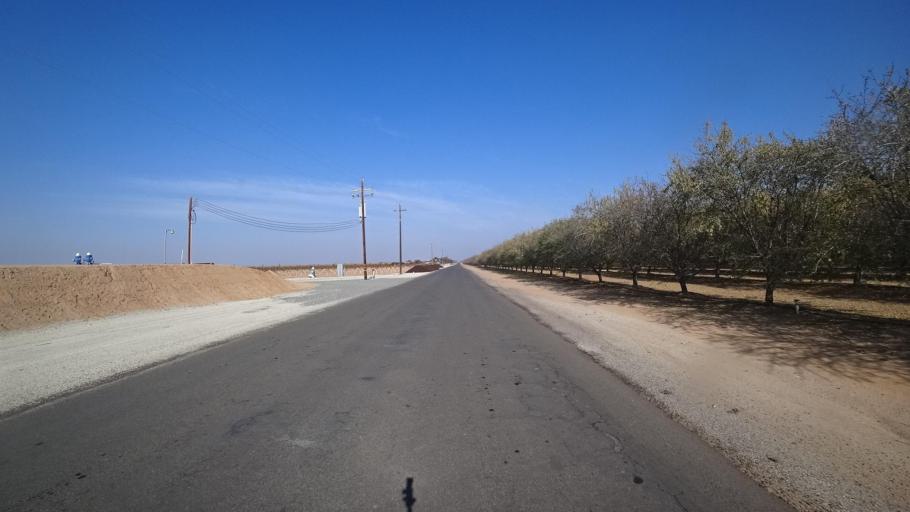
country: US
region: California
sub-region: Kern County
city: McFarland
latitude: 35.6344
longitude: -119.1866
